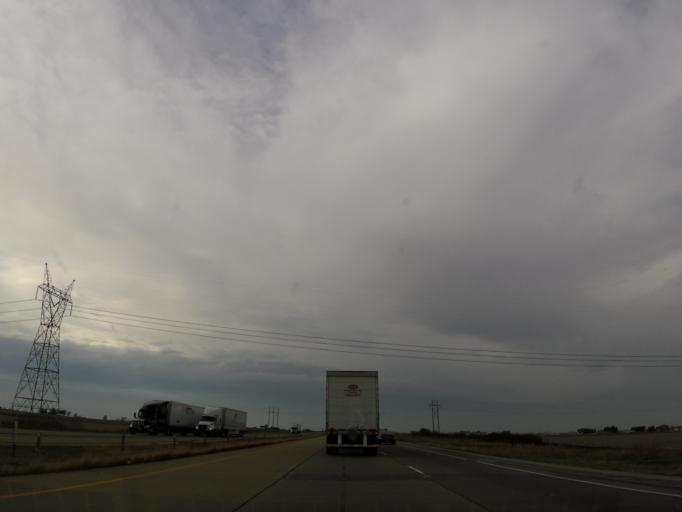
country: US
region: Iowa
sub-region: Scott County
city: Walcott
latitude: 41.6038
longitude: -90.6920
